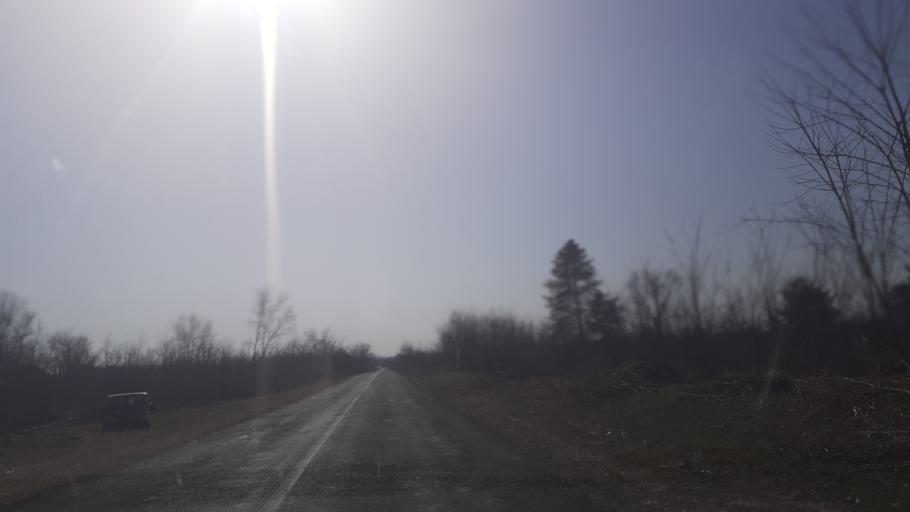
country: HU
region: Pest
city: Dabas
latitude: 47.1465
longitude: 19.3289
